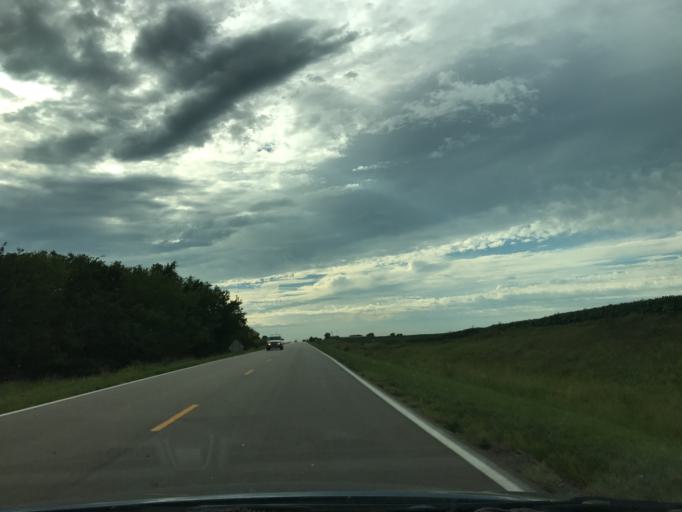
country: US
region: Nebraska
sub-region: Gage County
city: Beatrice
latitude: 40.2797
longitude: -96.7884
